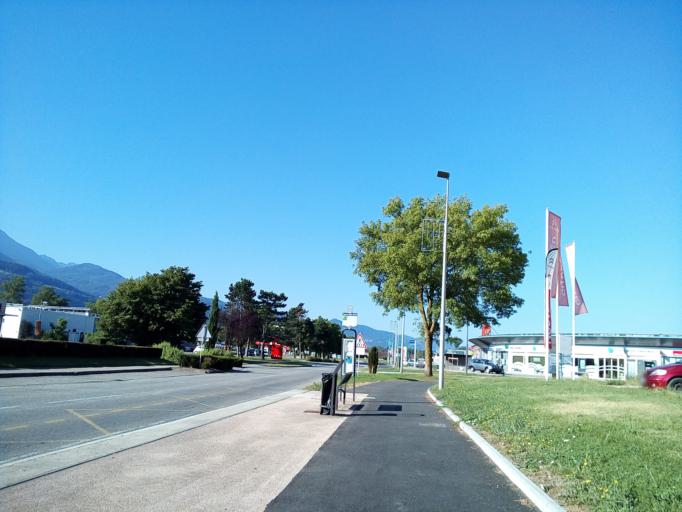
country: FR
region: Rhone-Alpes
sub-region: Departement de l'Isere
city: Crolles
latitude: 45.2724
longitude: 5.8931
